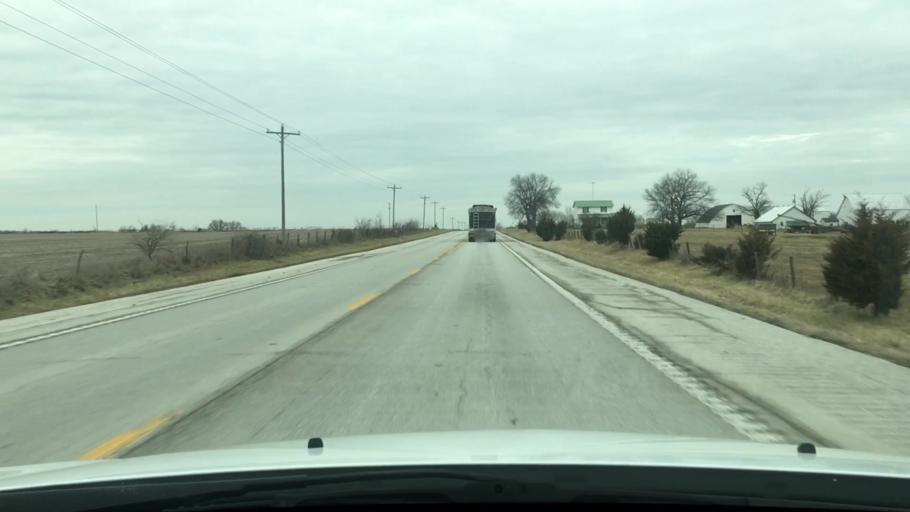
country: US
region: Missouri
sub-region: Montgomery County
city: Wellsville
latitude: 39.1749
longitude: -91.6476
